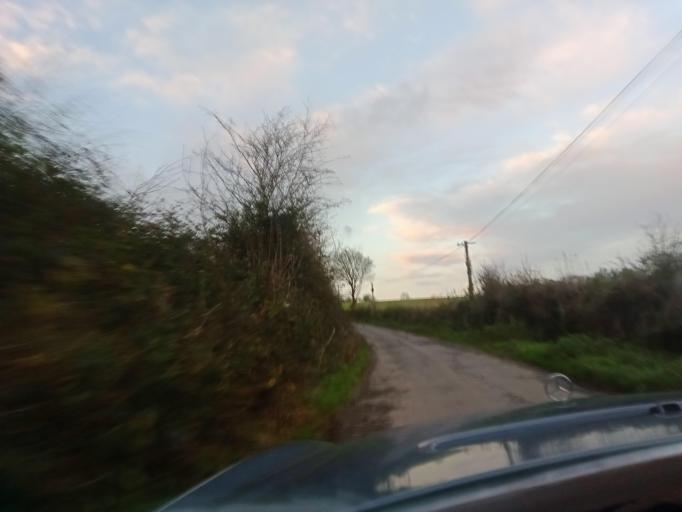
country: IE
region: Munster
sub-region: Waterford
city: Waterford
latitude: 52.3327
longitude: -7.0369
